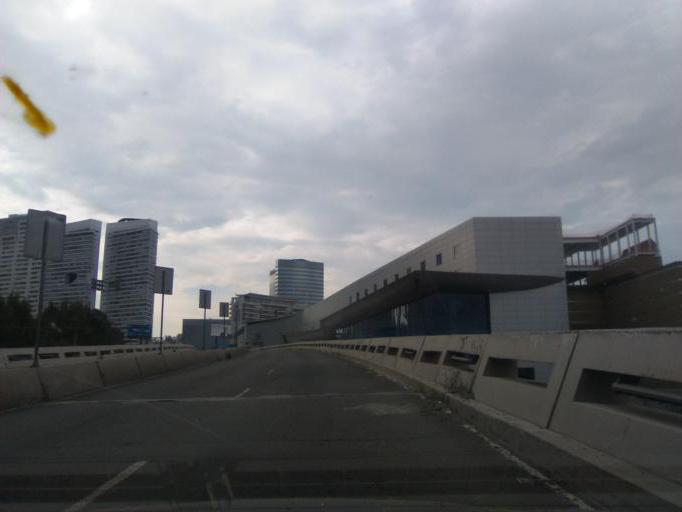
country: MX
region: Mexico City
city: Col. Bosques de las Lomas
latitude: 19.3617
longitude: -99.2620
